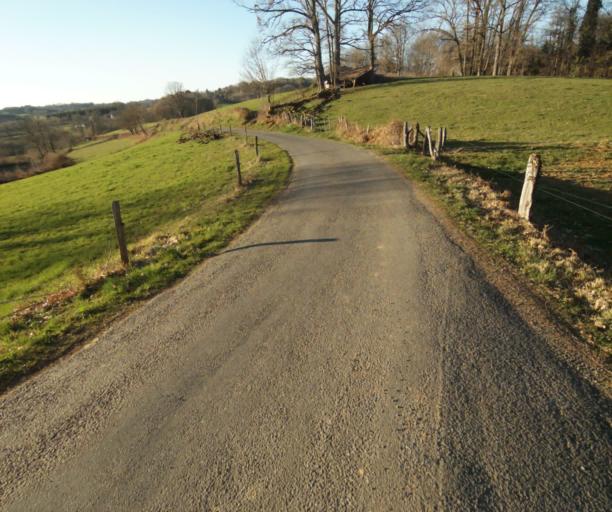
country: FR
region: Limousin
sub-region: Departement de la Correze
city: Saint-Clement
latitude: 45.3584
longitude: 1.6893
